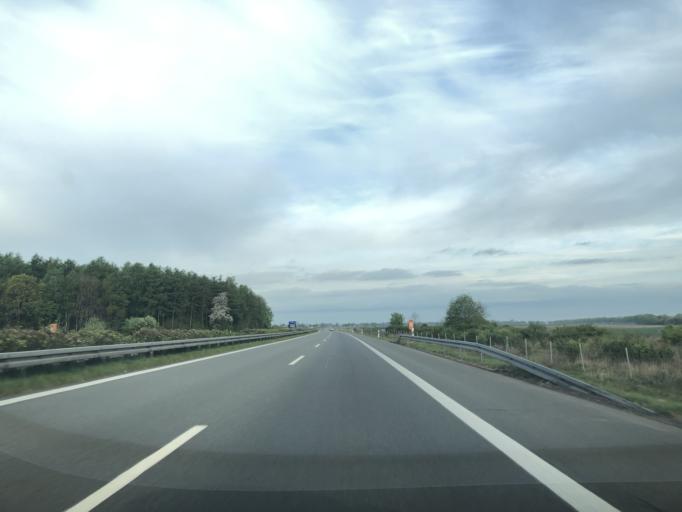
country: DE
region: Mecklenburg-Vorpommern
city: Tribsees
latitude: 54.0859
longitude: 12.8150
